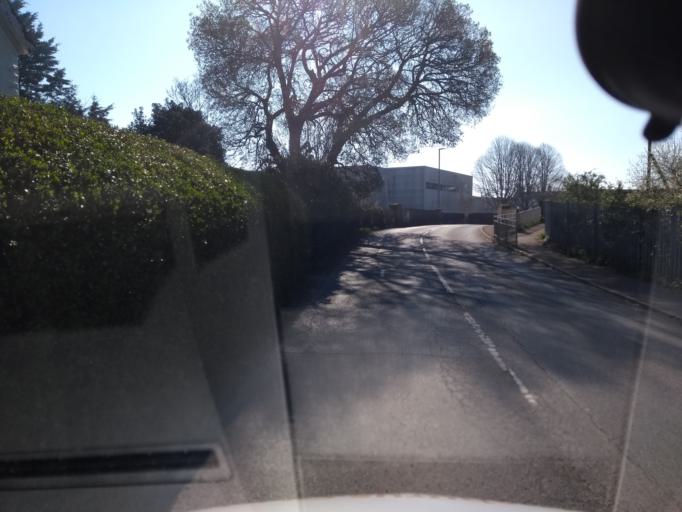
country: GB
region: England
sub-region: Somerset
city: Bishops Lydeard
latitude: 50.9851
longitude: -3.2399
